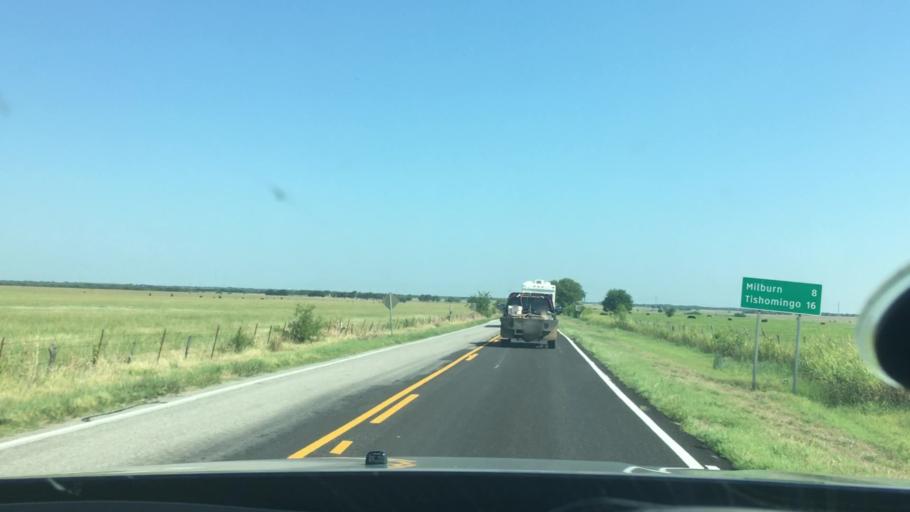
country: US
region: Oklahoma
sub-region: Johnston County
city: Tishomingo
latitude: 34.1459
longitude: -96.5045
